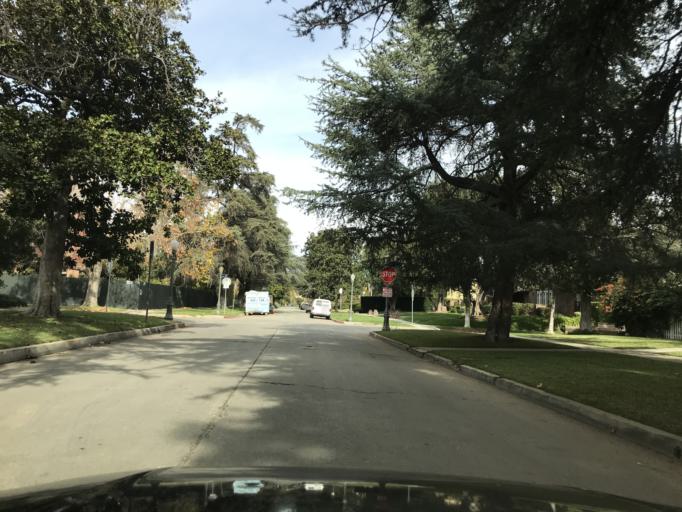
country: US
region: California
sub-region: Los Angeles County
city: Hollywood
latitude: 34.0665
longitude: -118.3200
